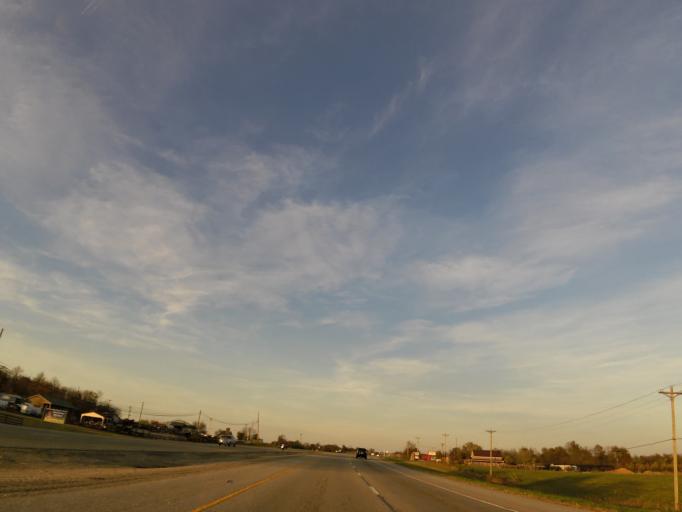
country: US
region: Kentucky
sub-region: Jessamine County
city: Nicholasville
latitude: 37.8195
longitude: -84.5966
